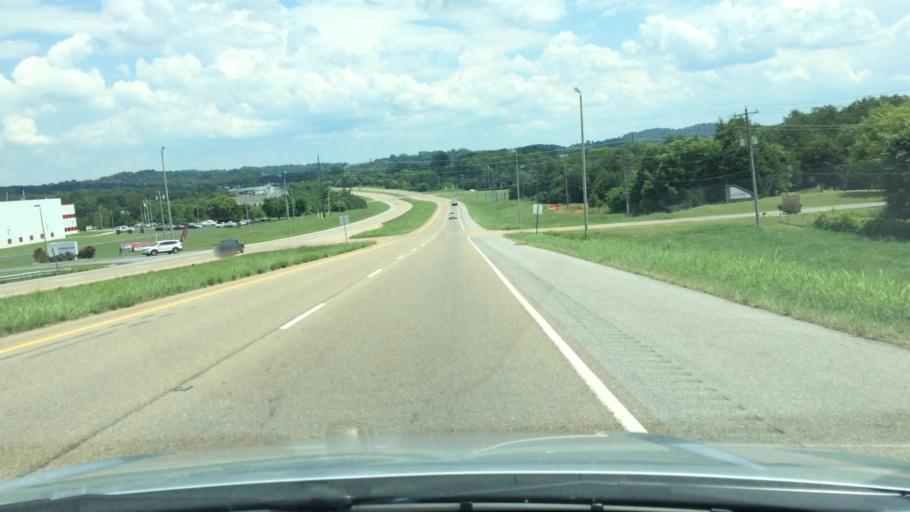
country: US
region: Tennessee
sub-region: Hamblen County
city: Morristown
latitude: 36.1688
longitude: -83.3821
